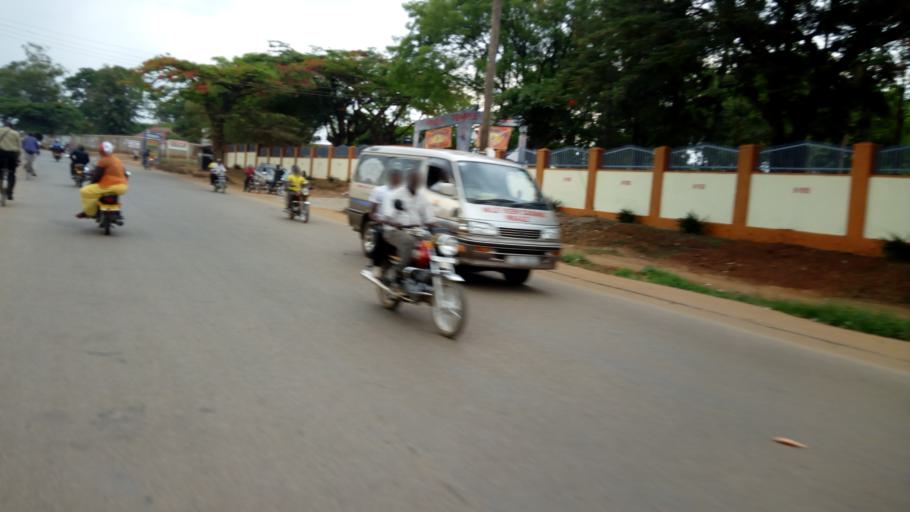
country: UG
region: Eastern Region
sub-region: Mbale District
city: Mbale
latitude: 1.0789
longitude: 34.1716
